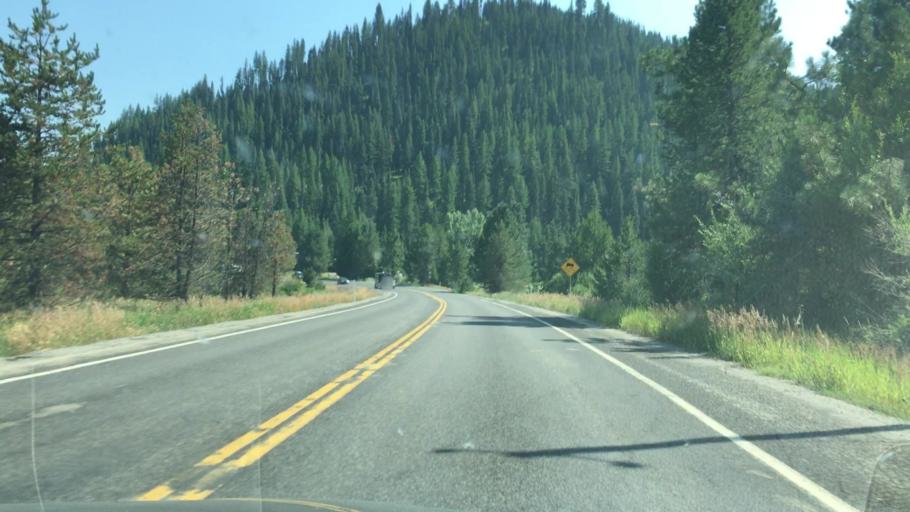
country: US
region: Idaho
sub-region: Valley County
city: Cascade
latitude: 44.3001
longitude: -116.0892
